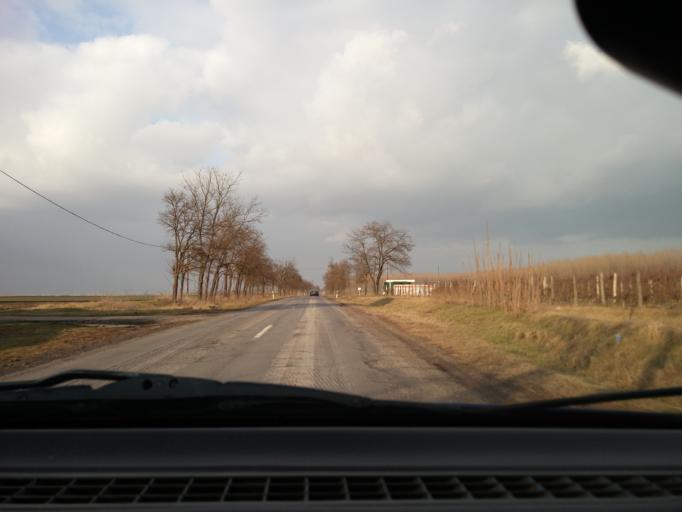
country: HU
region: Pest
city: Tapioszolos
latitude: 47.2971
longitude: 19.8687
